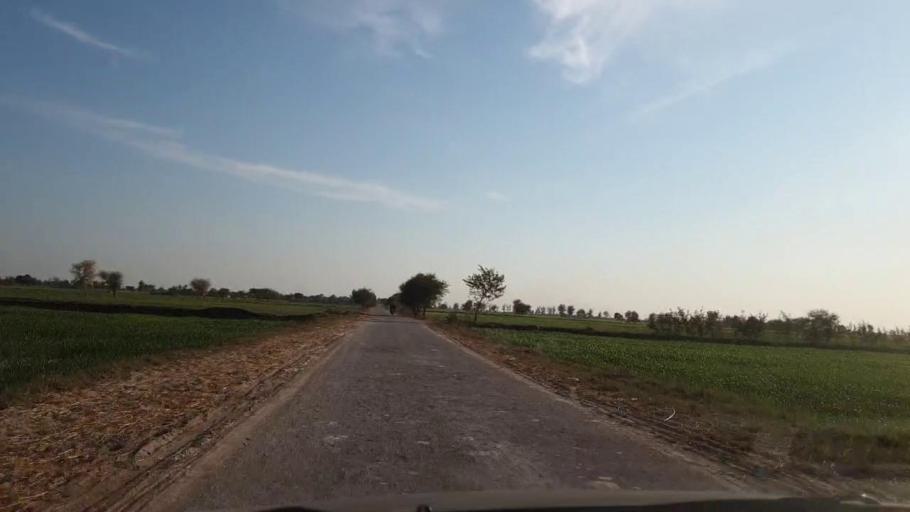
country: PK
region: Sindh
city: Khadro
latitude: 26.1971
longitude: 68.7468
